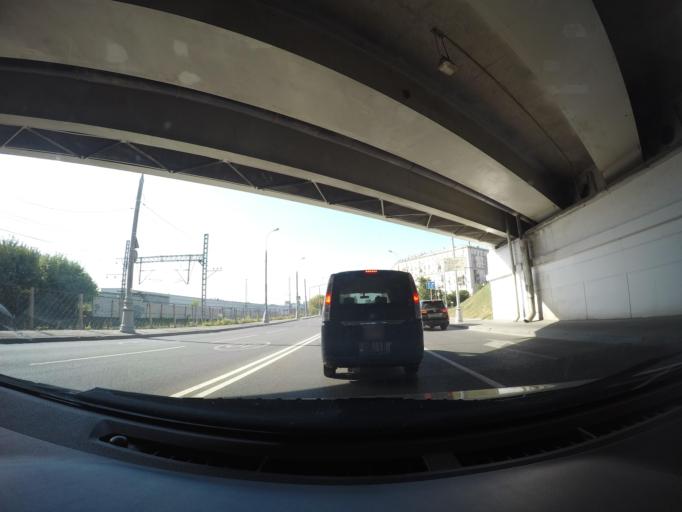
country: RU
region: Moscow
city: Mar'ina Roshcha
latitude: 55.7996
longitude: 37.6351
